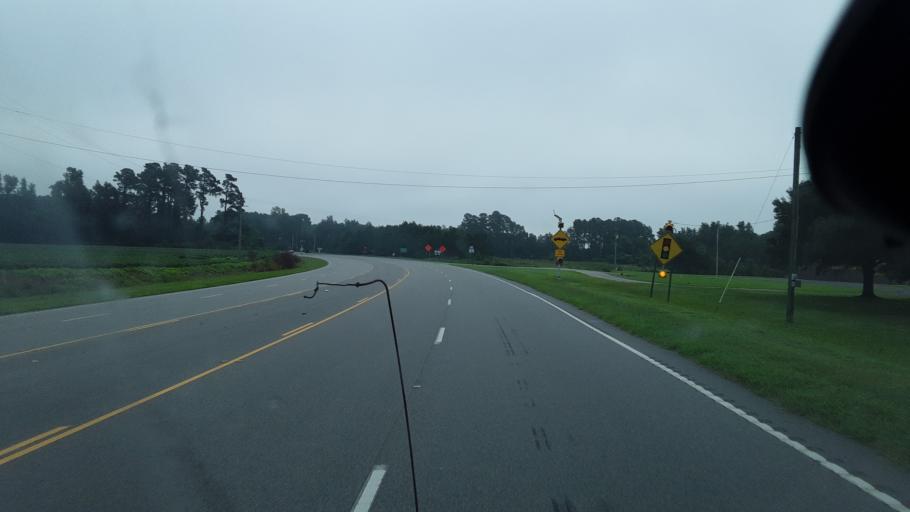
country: US
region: South Carolina
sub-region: Florence County
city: Johnsonville
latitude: 33.8817
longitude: -79.4572
